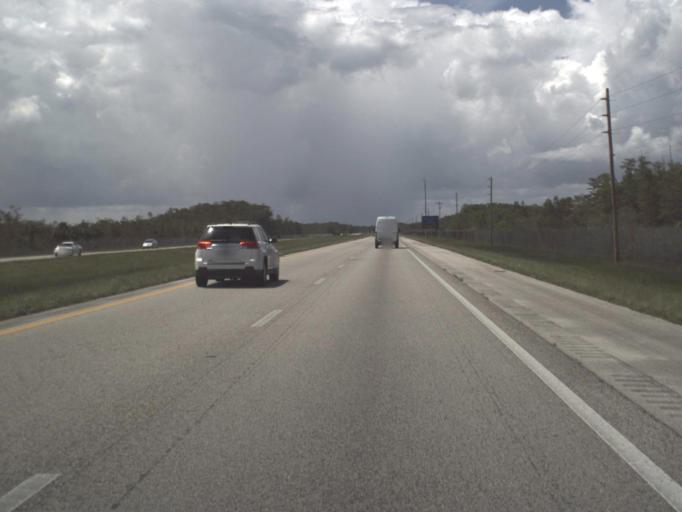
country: US
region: Florida
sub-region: Collier County
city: Immokalee
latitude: 26.1667
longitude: -81.2221
